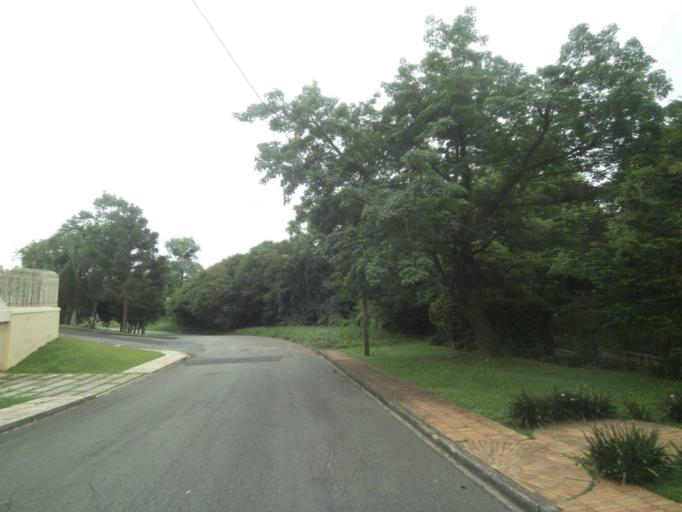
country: BR
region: Parana
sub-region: Curitiba
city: Curitiba
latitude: -25.4014
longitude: -49.2916
